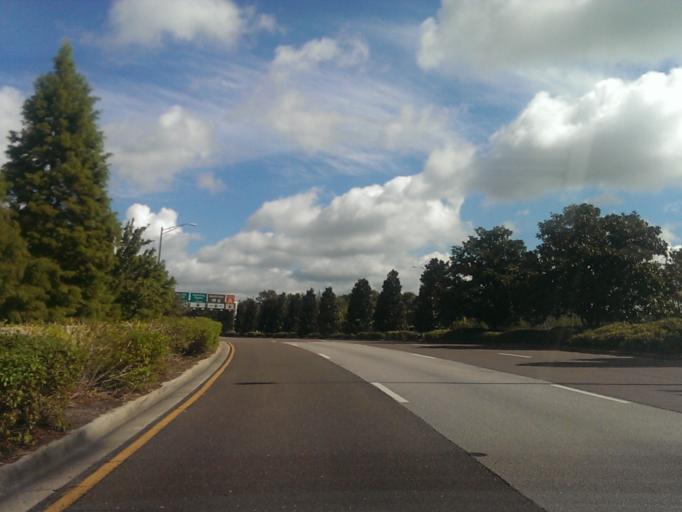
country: US
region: Florida
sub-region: Orange County
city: Taft
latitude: 28.4270
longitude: -81.3068
